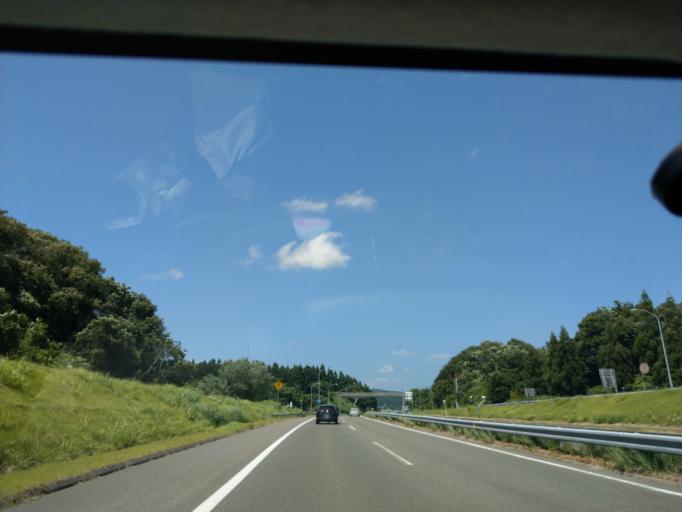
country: JP
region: Akita
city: Omagari
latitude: 39.5412
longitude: 140.3233
